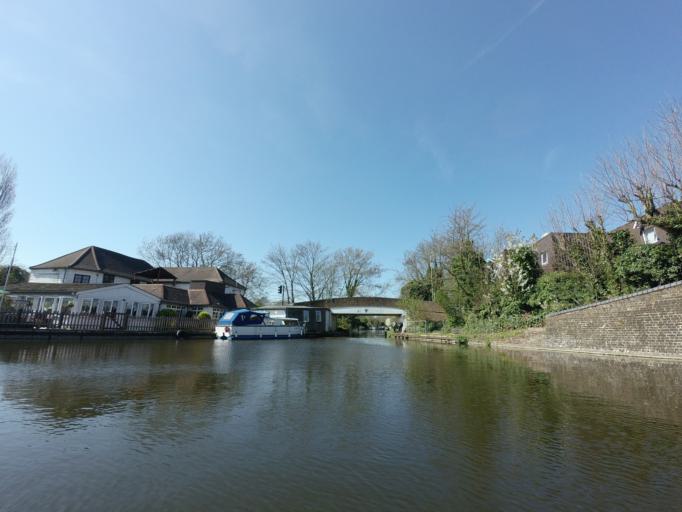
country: GB
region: England
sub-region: Greater London
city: West Drayton
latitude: 51.5199
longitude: -0.4826
